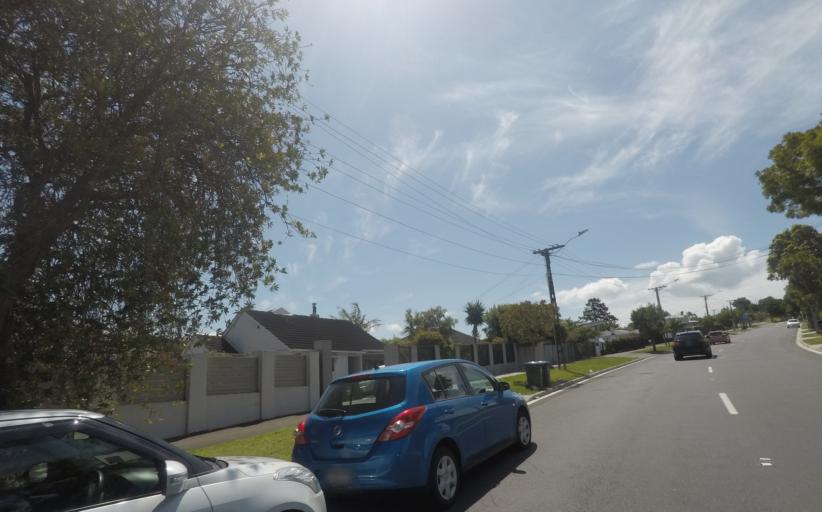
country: NZ
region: Auckland
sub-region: Auckland
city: Tamaki
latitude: -36.8702
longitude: 174.8501
